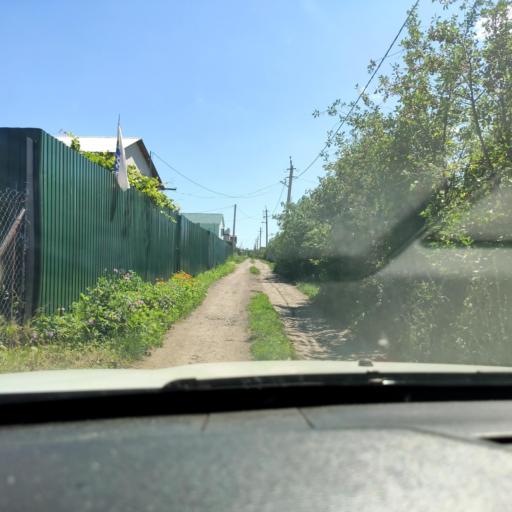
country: RU
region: Samara
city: Dubovyy Umet
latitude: 53.0294
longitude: 50.2492
